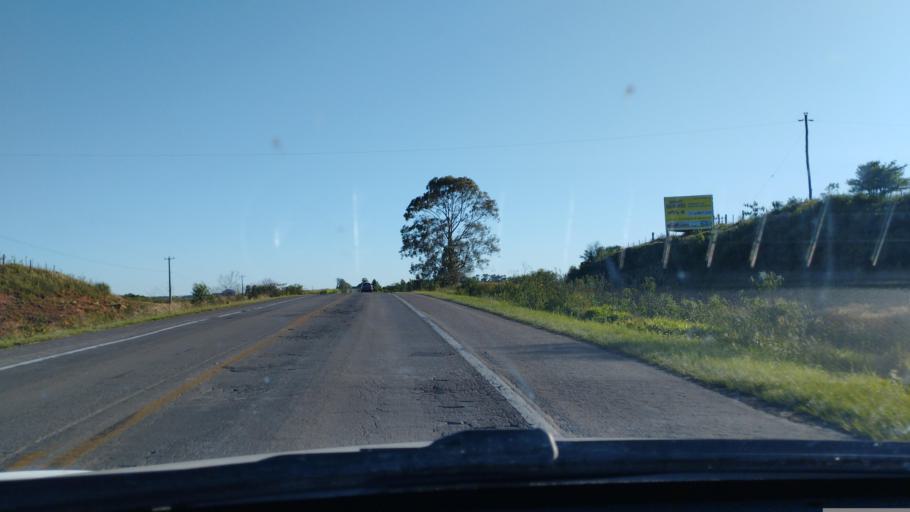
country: BR
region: Rio Grande do Sul
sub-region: Julio De Castilhos
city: Julio de Castilhos
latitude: -29.4150
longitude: -53.6704
